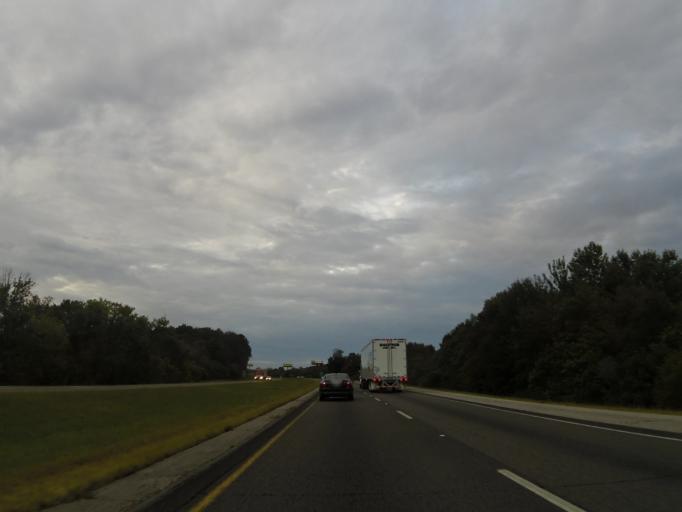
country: US
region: Alabama
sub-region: Jefferson County
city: Argo
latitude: 33.6826
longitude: -86.5357
